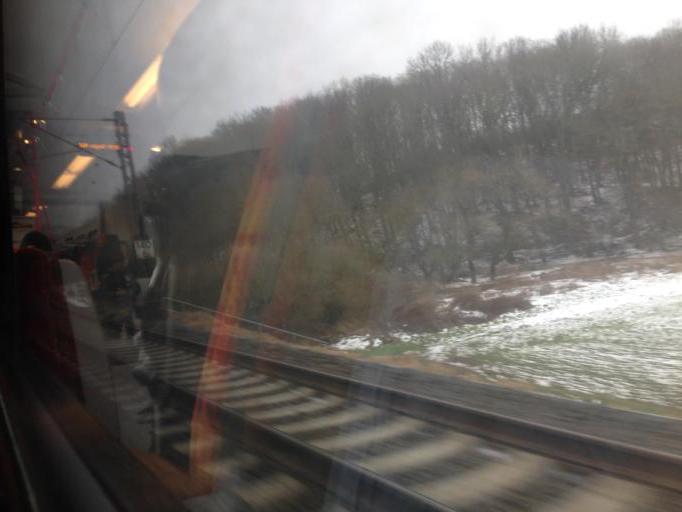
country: DE
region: Hesse
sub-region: Regierungsbezirk Giessen
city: Ehringshausen
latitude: 50.6135
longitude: 8.3598
